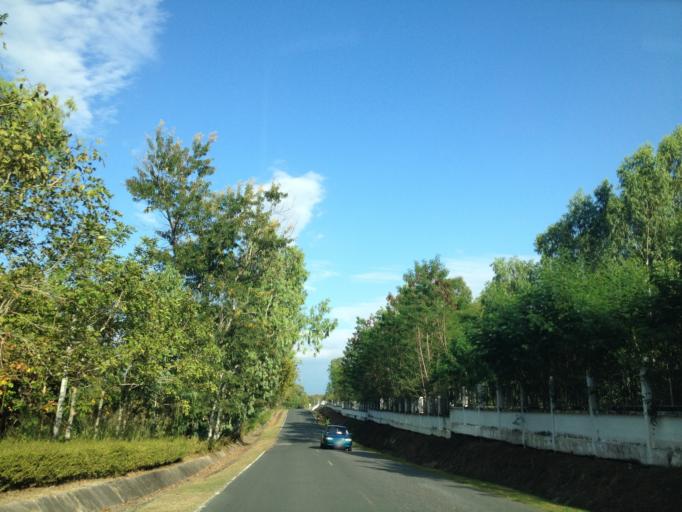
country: TH
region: Chiang Mai
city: Chiang Mai
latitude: 18.8585
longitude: 98.9547
